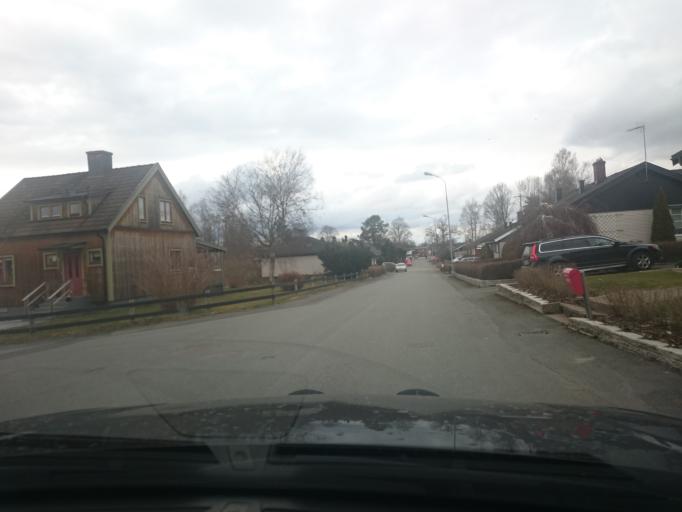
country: SE
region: Joenkoeping
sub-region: Vetlanda Kommun
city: Vetlanda
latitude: 57.2978
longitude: 15.1266
